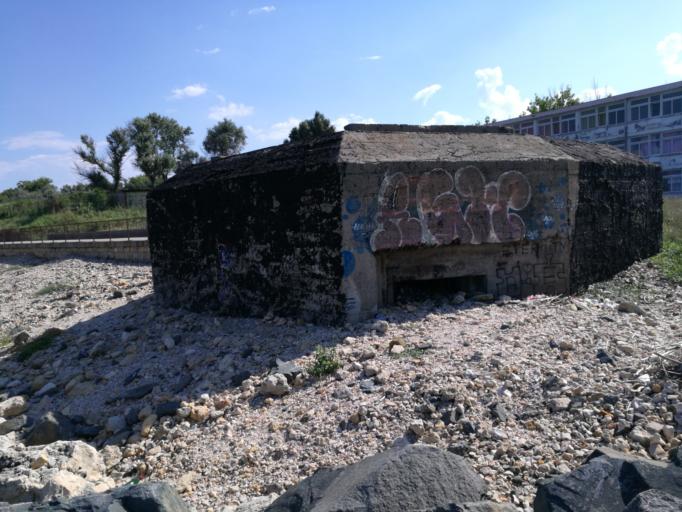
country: RO
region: Constanta
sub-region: Oras Eforie
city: Eforie
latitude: 44.0434
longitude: 28.6475
